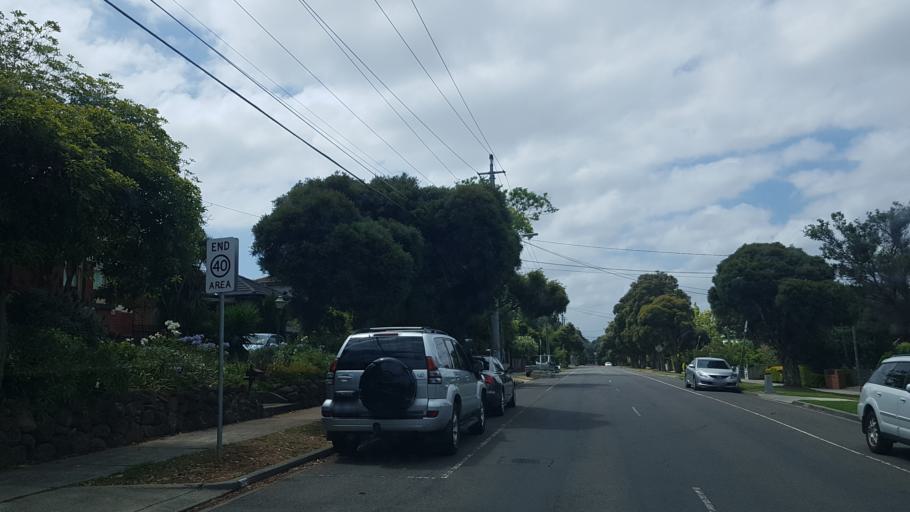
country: AU
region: Victoria
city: Rosanna
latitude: -37.7540
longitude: 145.0676
